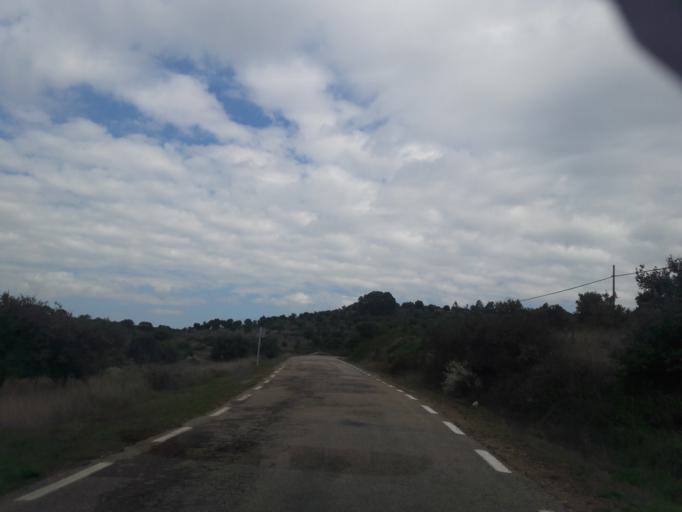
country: ES
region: Castille and Leon
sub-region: Provincia de Salamanca
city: Serradilla del Arroyo
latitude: 40.5257
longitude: -6.3822
